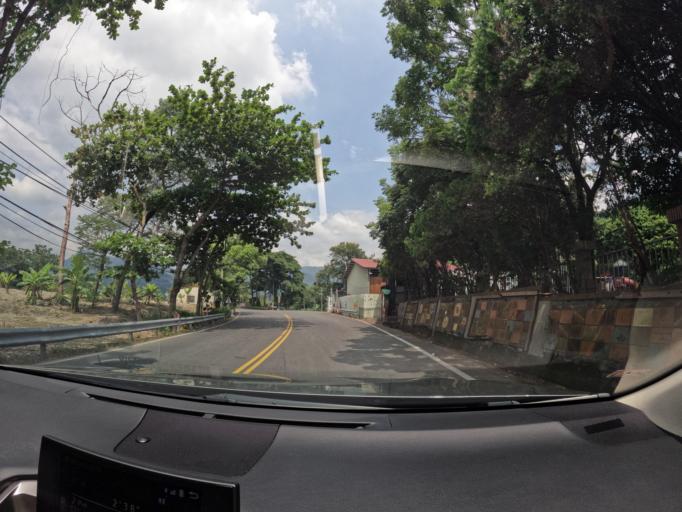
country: TW
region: Taiwan
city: Lugu
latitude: 23.8063
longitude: 120.8380
